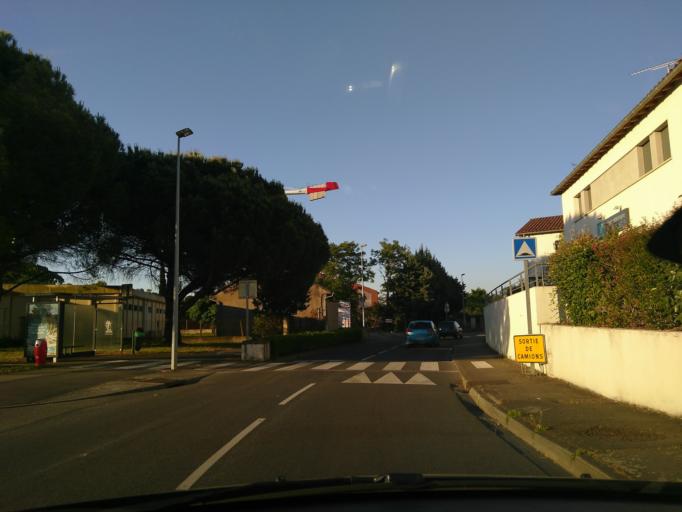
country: FR
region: Midi-Pyrenees
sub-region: Departement de la Haute-Garonne
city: Aussonne
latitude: 43.6852
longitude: 1.3215
